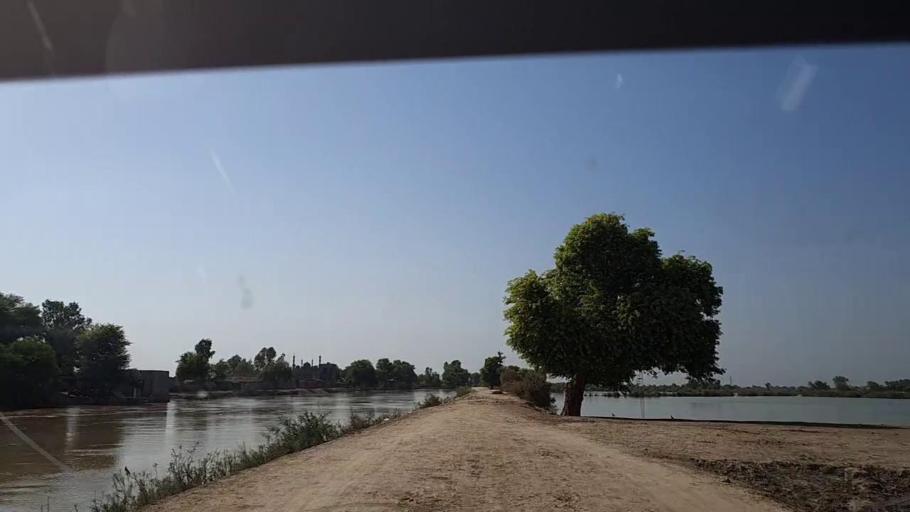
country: PK
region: Sindh
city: Ghauspur
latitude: 28.1796
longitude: 69.0889
